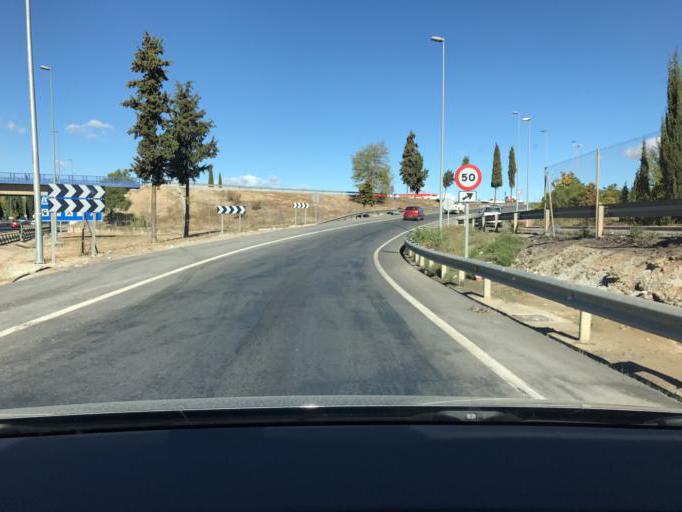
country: ES
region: Andalusia
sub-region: Provincia de Granada
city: Peligros
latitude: 37.2280
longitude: -3.6367
